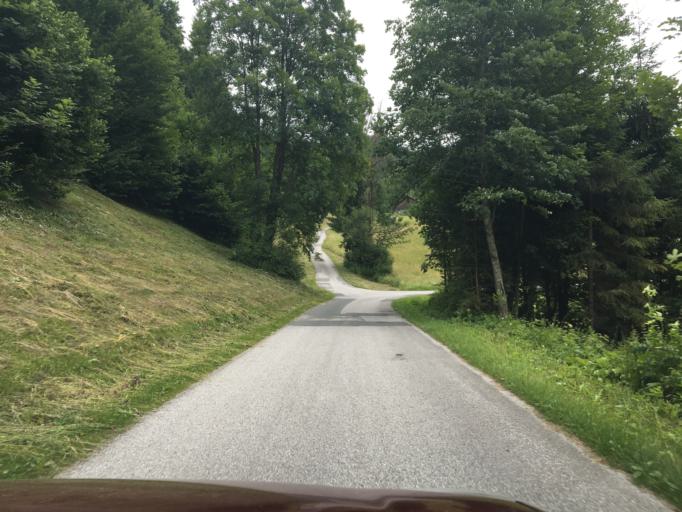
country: AT
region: Salzburg
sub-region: Politischer Bezirk Hallein
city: Scheffau am Tennengebirge
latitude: 47.6249
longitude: 13.2331
